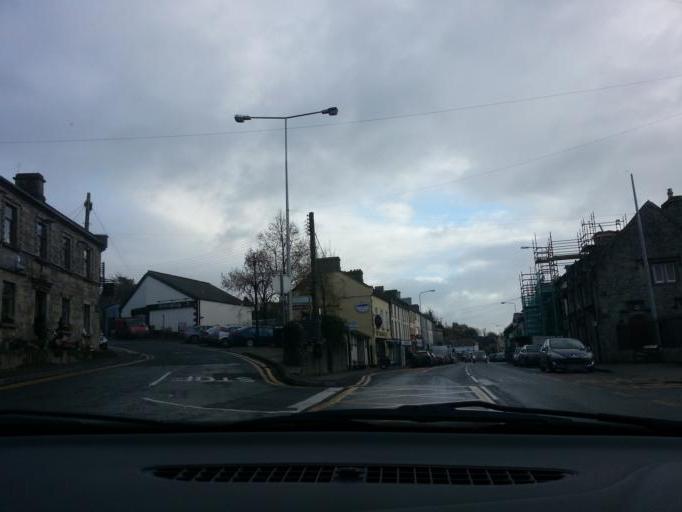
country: GB
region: Northern Ireland
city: Lisnaskea
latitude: 54.2529
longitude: -7.4429
